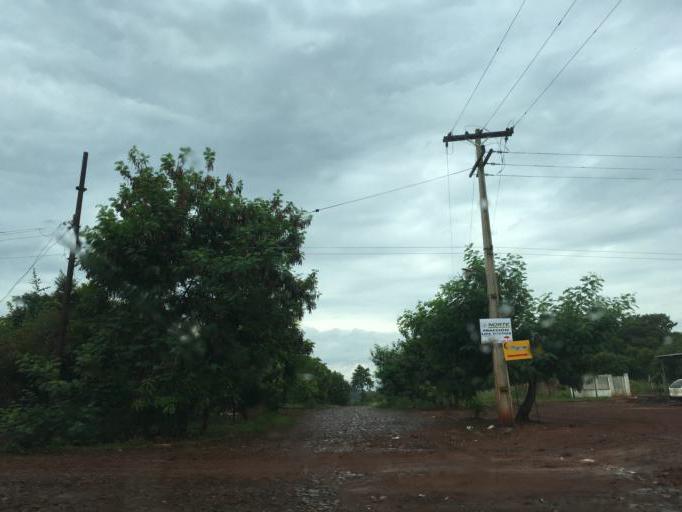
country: PY
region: Alto Parana
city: Ciudad del Este
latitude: -25.4383
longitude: -54.6543
